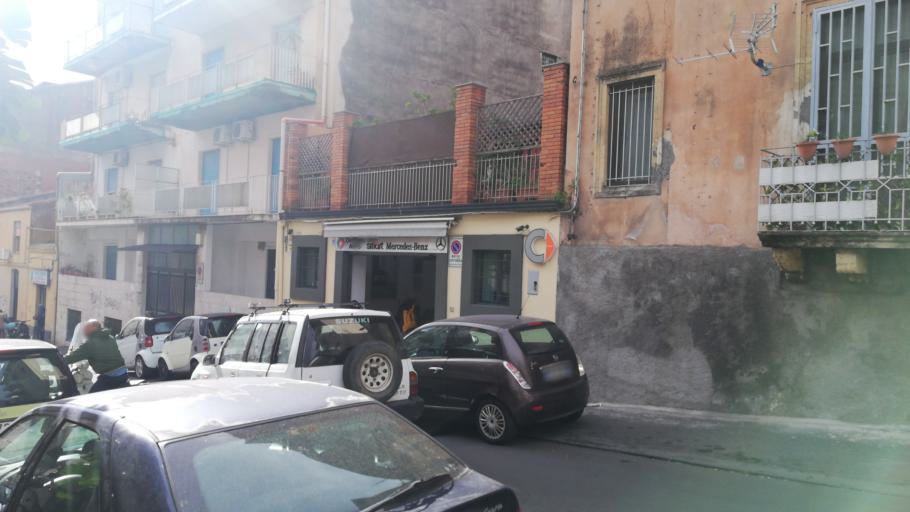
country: IT
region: Sicily
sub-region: Catania
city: Canalicchio
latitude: 37.5199
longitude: 15.0843
